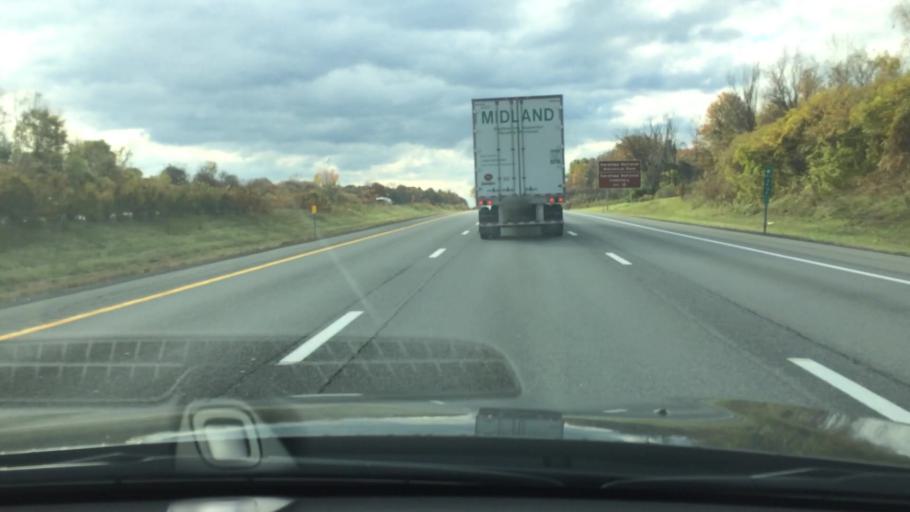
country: US
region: New York
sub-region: Saratoga County
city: Ballston Spa
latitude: 42.9854
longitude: -73.8035
